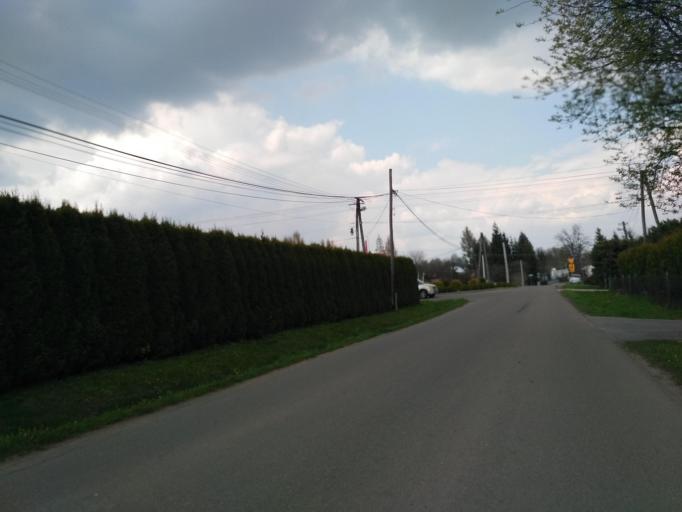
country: PL
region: Subcarpathian Voivodeship
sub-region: Powiat brzozowski
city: Humniska
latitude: 49.6710
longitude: 22.0312
